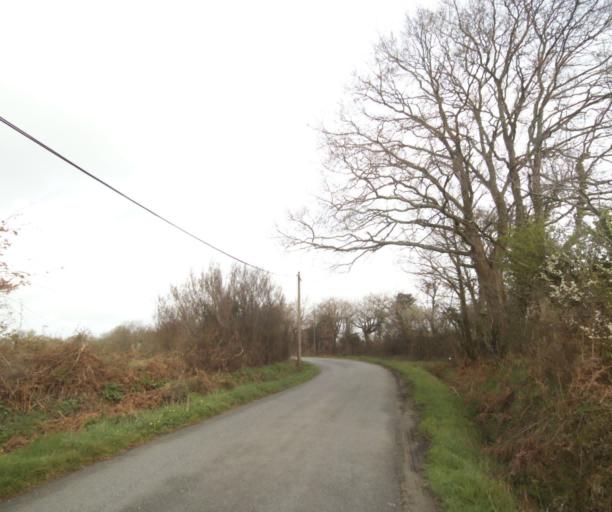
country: FR
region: Pays de la Loire
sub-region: Departement de la Loire-Atlantique
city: Bouvron
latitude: 47.4030
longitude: -1.8625
